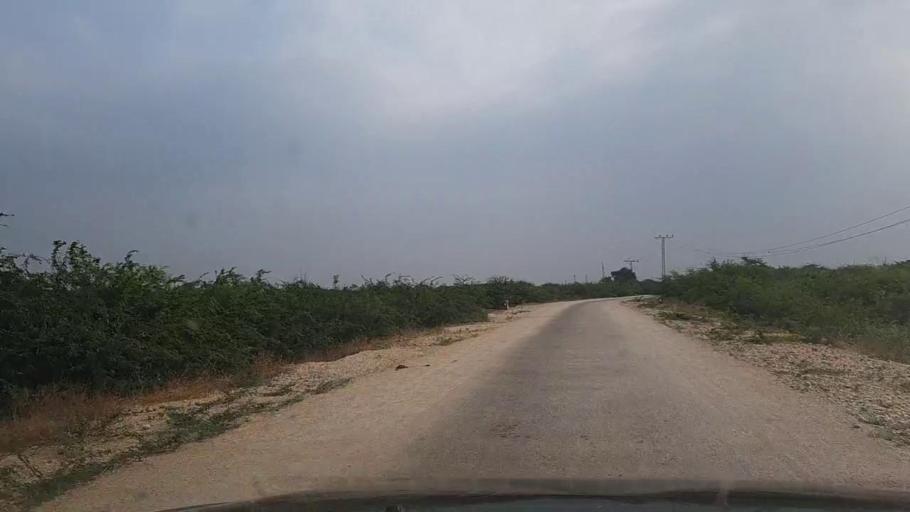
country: PK
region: Sindh
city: Thatta
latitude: 24.8484
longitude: 67.7777
